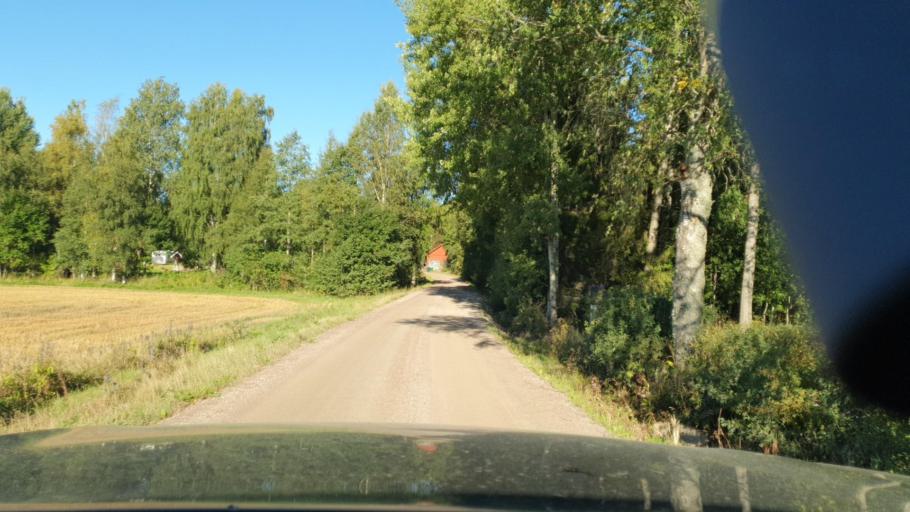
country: SE
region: Vaermland
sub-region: Karlstads Kommun
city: Molkom
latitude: 59.5230
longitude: 13.9160
